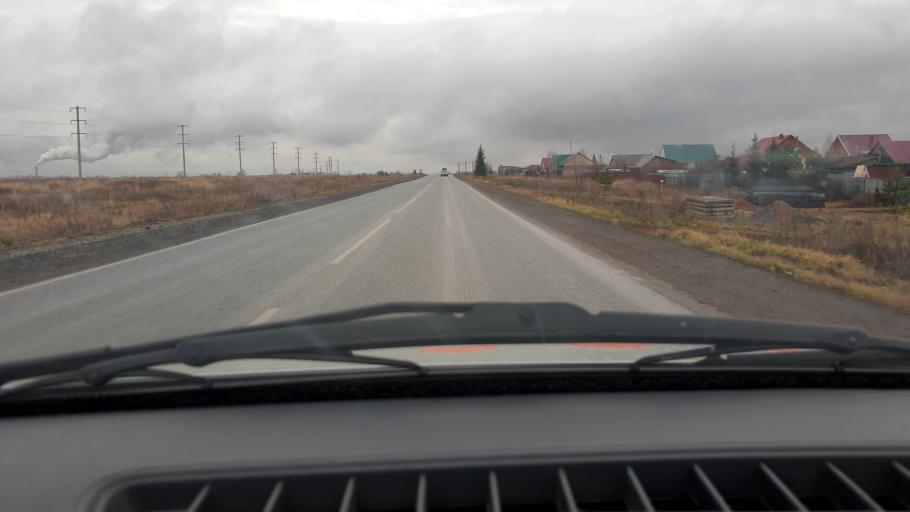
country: RU
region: Bashkortostan
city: Iglino
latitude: 54.7839
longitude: 56.2528
